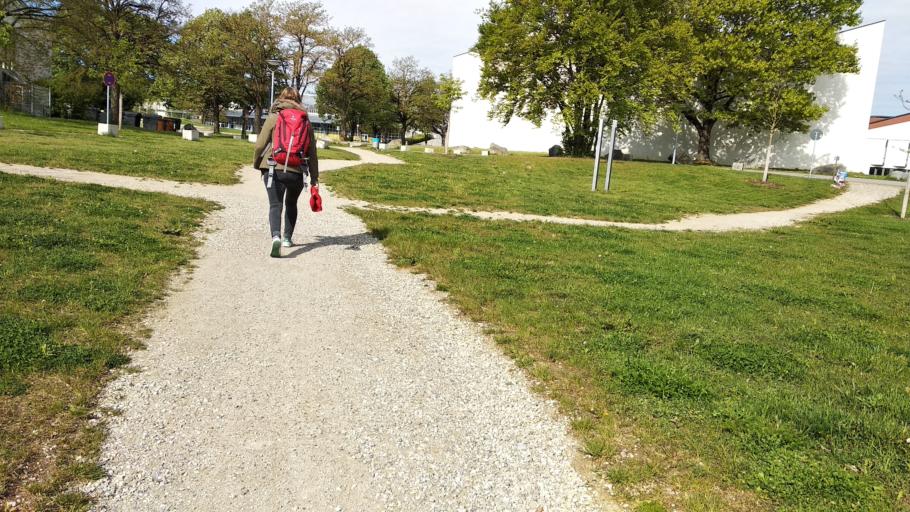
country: DE
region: Bavaria
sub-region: Upper Bavaria
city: Freising
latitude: 48.3994
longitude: 11.7265
